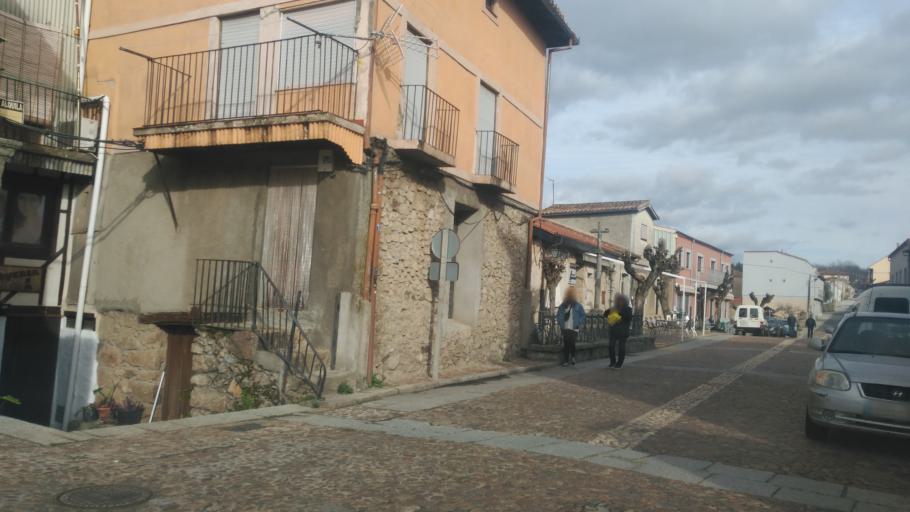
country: ES
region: Castille and Leon
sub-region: Provincia de Salamanca
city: Miranda del Castanar
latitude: 40.4844
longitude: -5.9986
